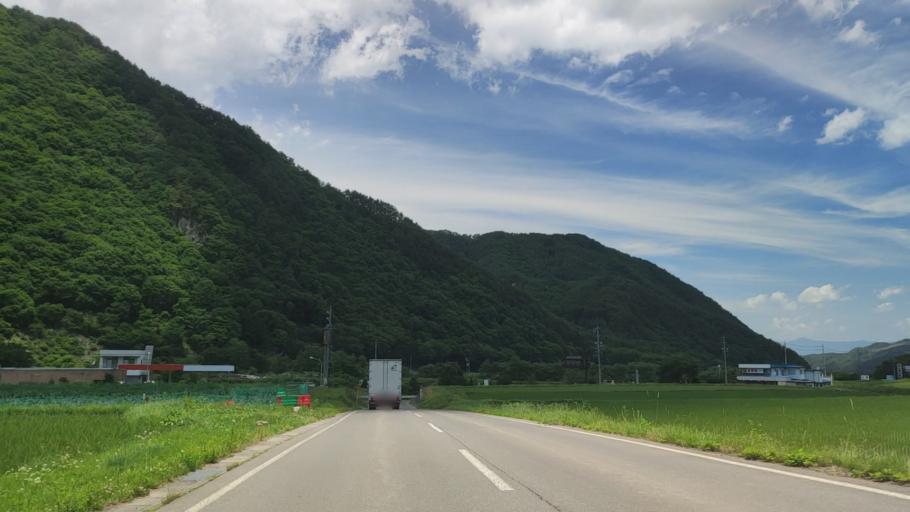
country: JP
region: Nagano
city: Kamimaruko
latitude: 36.2426
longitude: 138.2587
